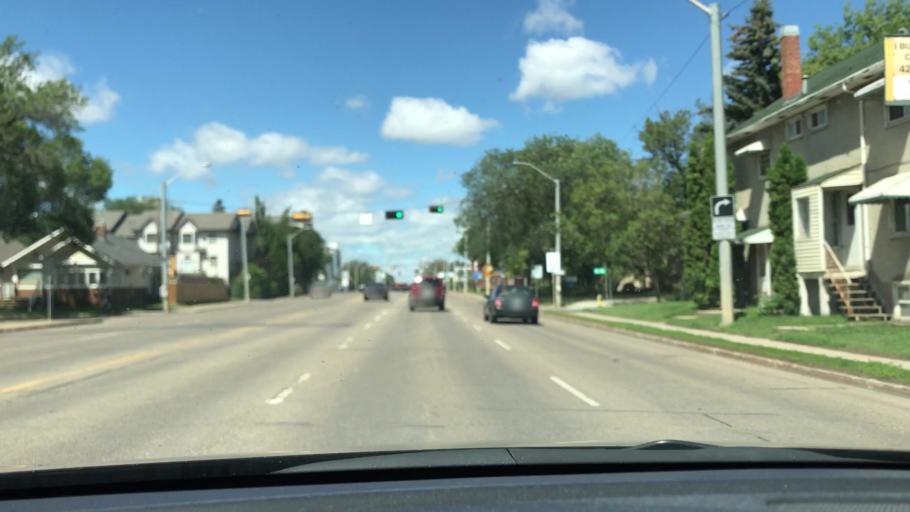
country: CA
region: Alberta
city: Edmonton
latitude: 53.5157
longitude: -113.5120
